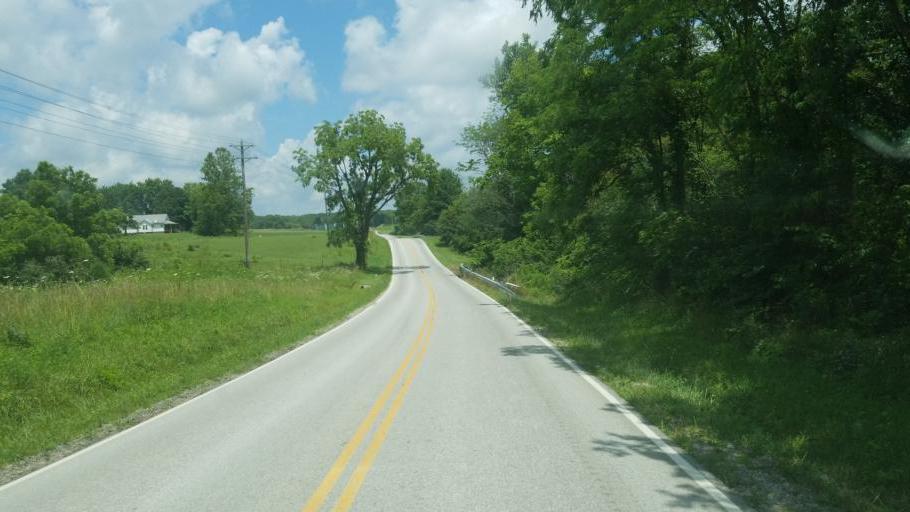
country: US
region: Ohio
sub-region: Highland County
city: Leesburg
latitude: 39.2559
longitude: -83.4738
